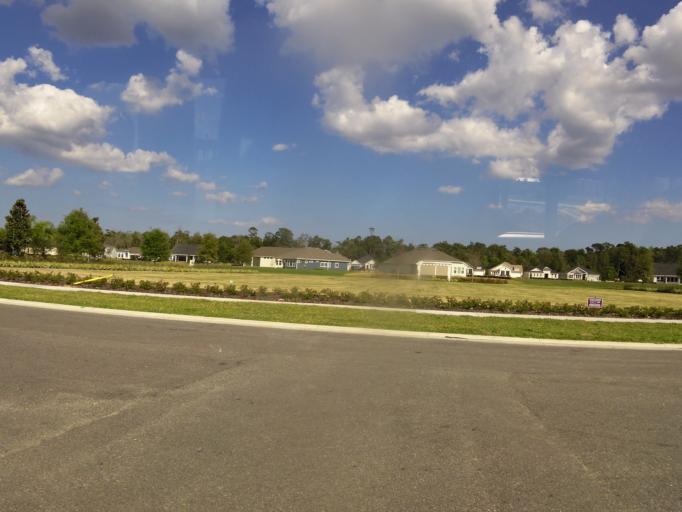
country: US
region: Florida
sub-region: Saint Johns County
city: Palm Valley
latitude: 30.1738
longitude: -81.5054
